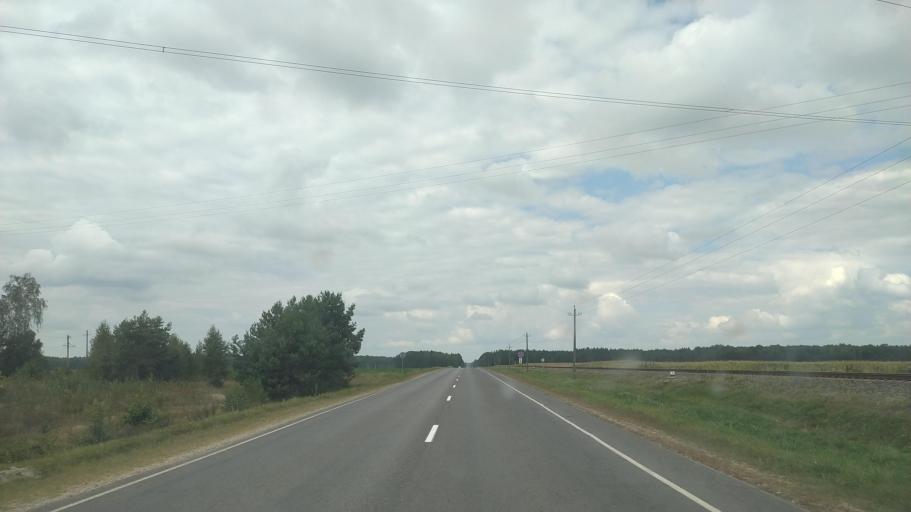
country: BY
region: Brest
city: Byelaazyorsk
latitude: 52.5148
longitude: 25.1542
